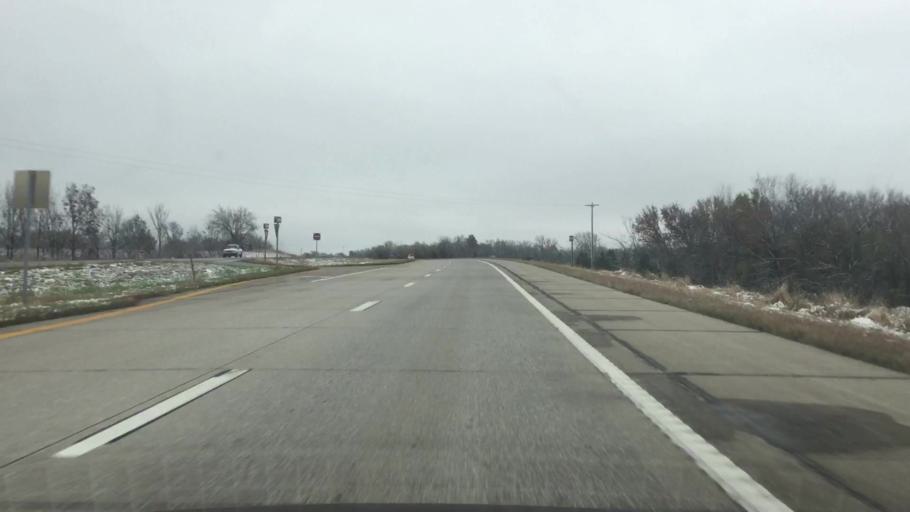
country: US
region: Missouri
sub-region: Saint Clair County
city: Osceola
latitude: 38.1906
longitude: -93.7405
